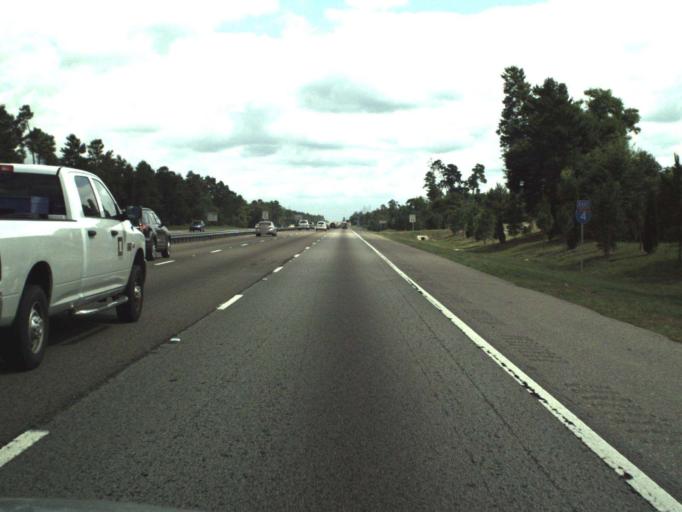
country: US
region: Florida
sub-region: Volusia County
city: Deltona
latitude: 28.9201
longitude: -81.2687
